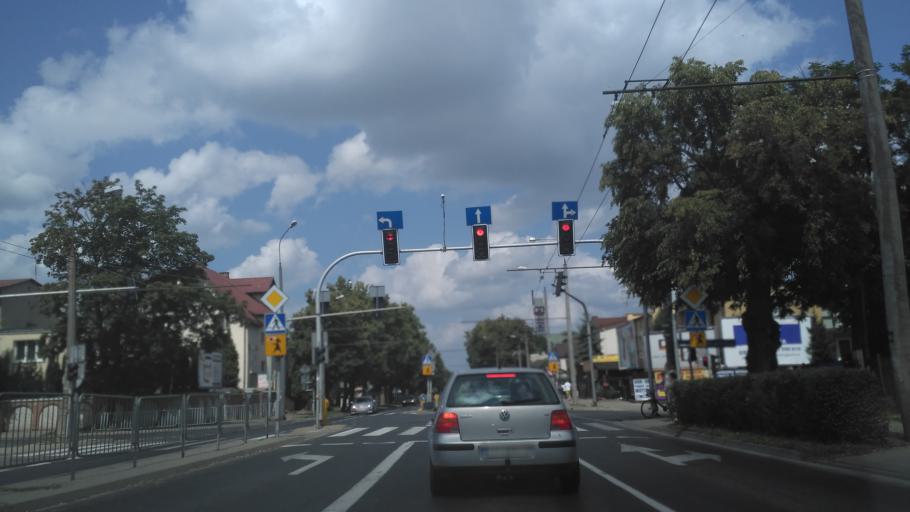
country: PL
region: Lublin Voivodeship
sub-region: Powiat lubelski
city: Lublin
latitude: 51.2172
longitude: 22.5802
